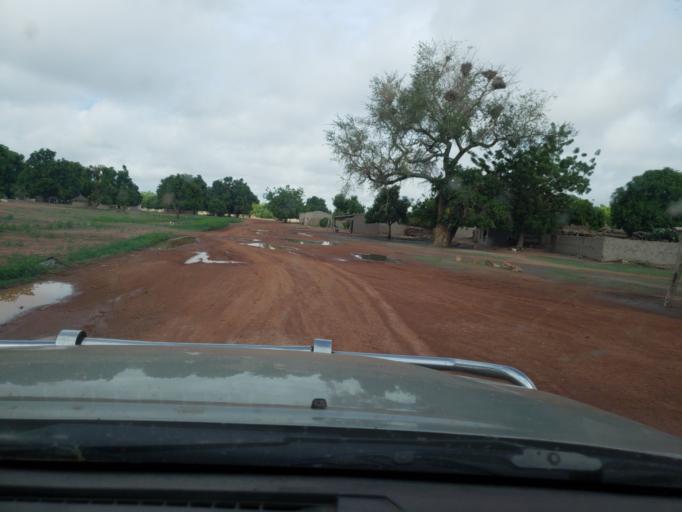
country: ML
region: Sikasso
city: Koutiala
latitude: 12.3922
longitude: -6.0236
